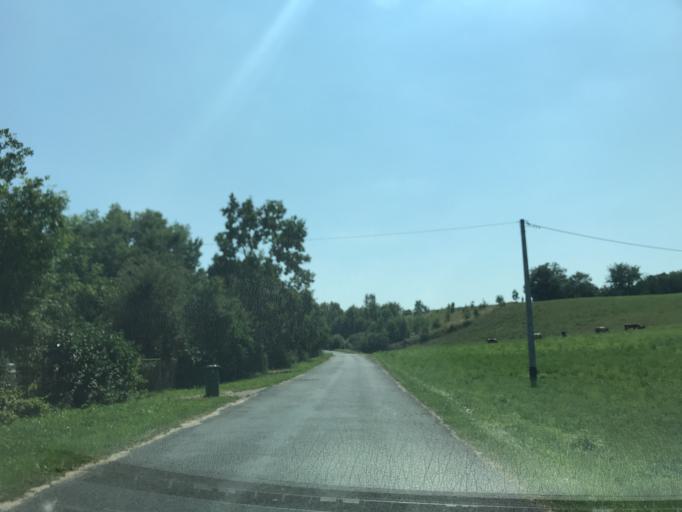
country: PL
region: Kujawsko-Pomorskie
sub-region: Powiat golubsko-dobrzynski
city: Zbojno
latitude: 52.9927
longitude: 19.2116
